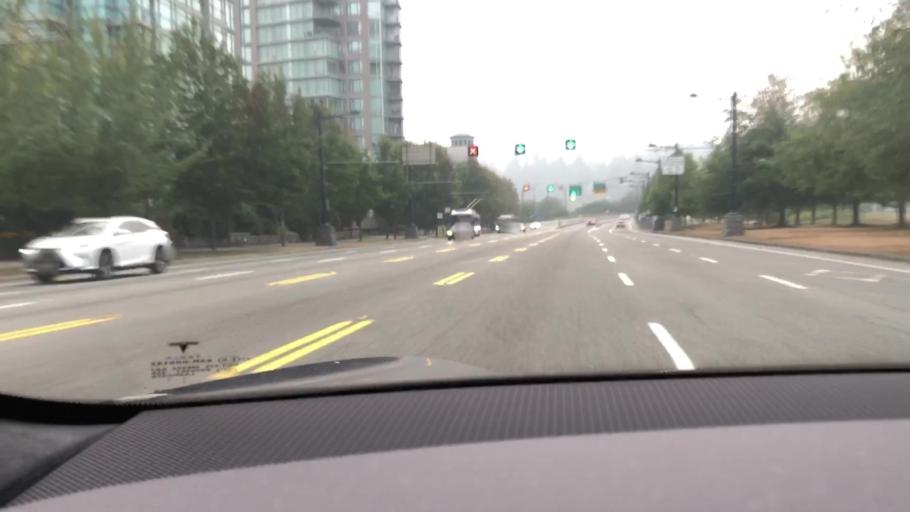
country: CA
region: British Columbia
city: West End
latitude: 49.2930
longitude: -123.1343
